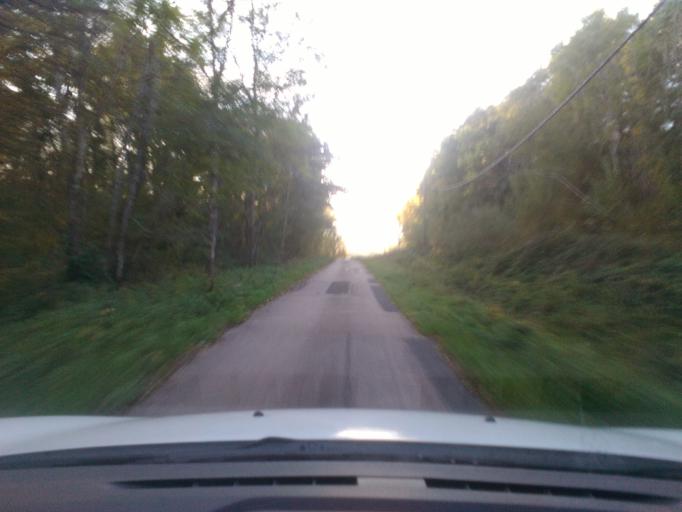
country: FR
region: Lorraine
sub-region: Departement des Vosges
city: Charmes
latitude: 48.3374
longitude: 6.2561
